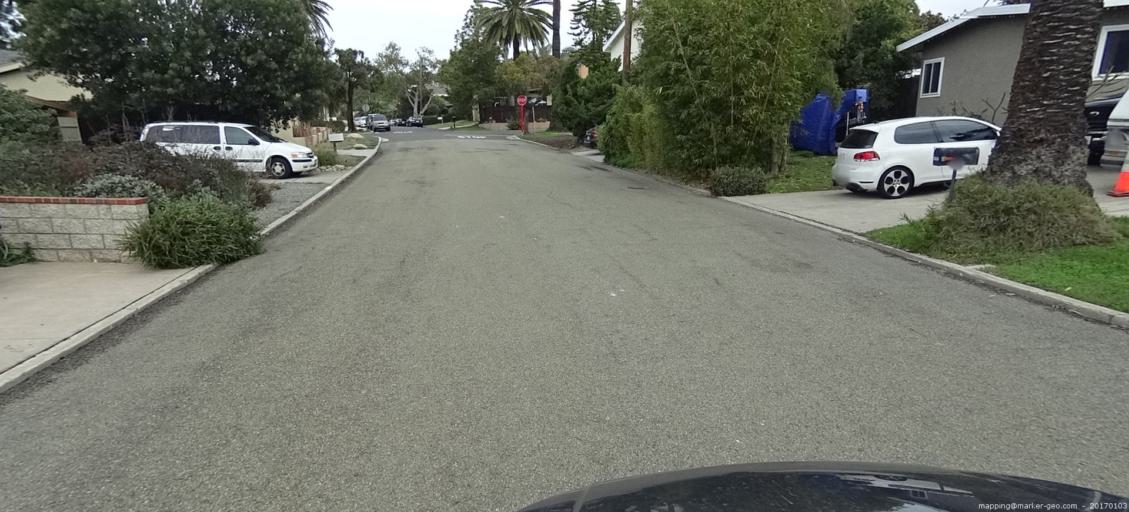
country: US
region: California
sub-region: Orange County
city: Dana Point
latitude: 33.4589
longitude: -117.6613
